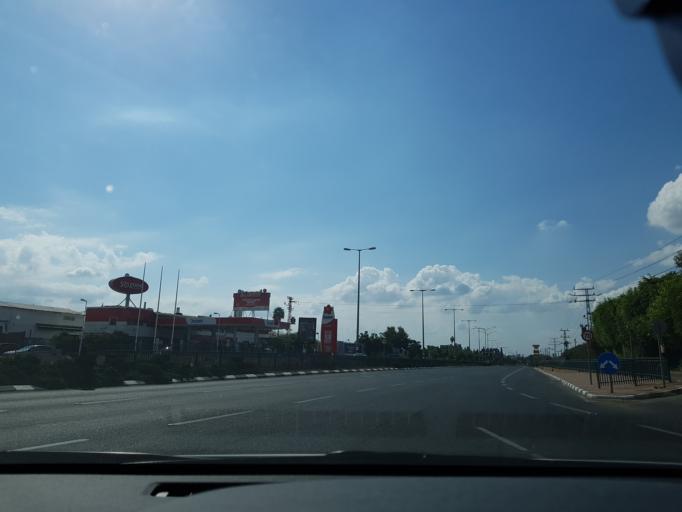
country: IL
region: Central District
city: Ness Ziona
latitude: 31.9478
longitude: 34.8013
